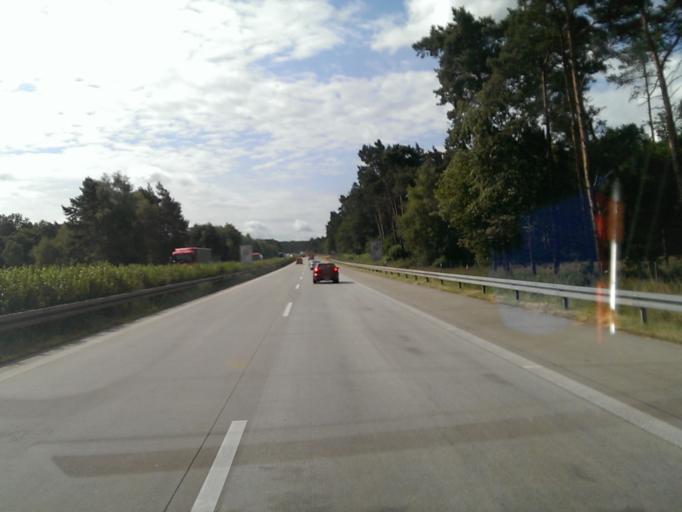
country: DE
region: Brandenburg
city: Bestensee
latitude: 52.2310
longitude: 13.5939
